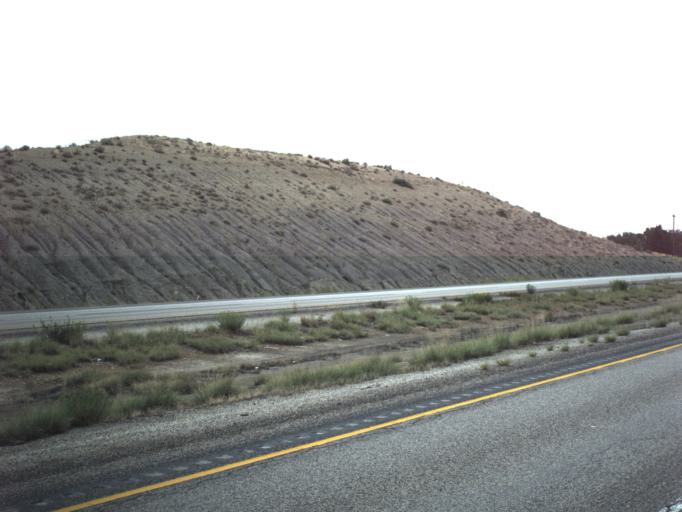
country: US
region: Utah
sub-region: Carbon County
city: Carbonville
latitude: 39.6114
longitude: -110.8360
